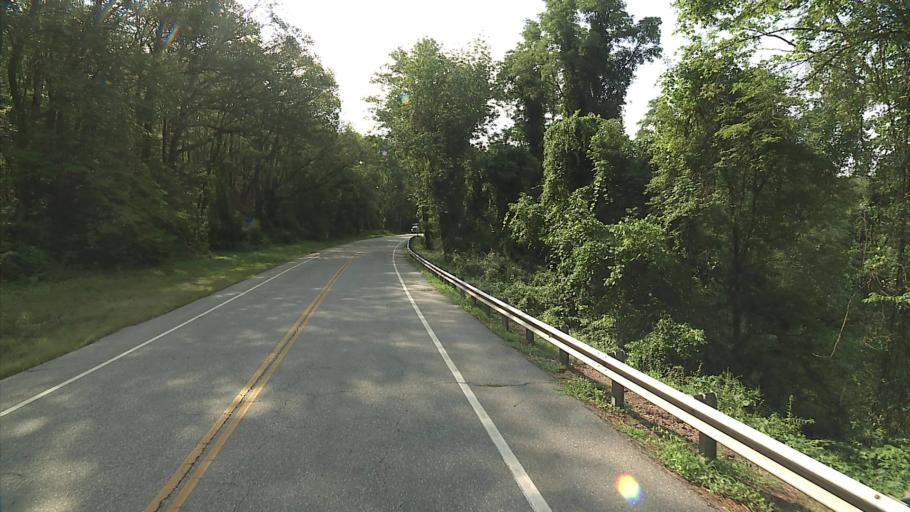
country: US
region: Connecticut
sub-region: Middlesex County
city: East Haddam
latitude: 41.4700
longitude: -72.4671
